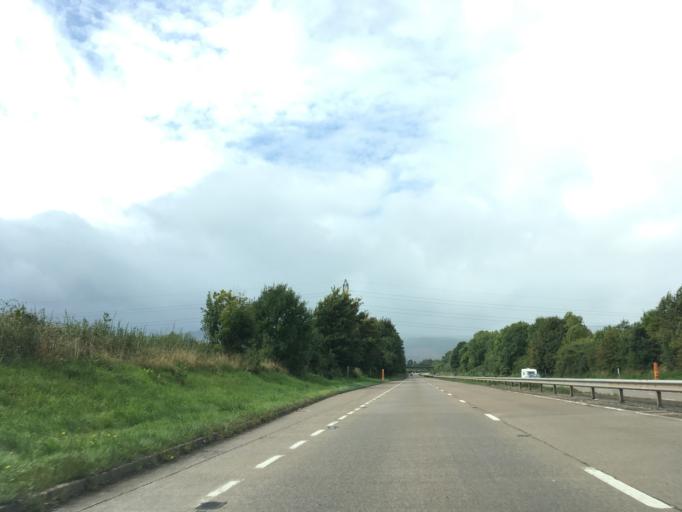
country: GB
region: Wales
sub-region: Monmouthshire
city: Llanarth
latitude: 51.7844
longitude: -2.9633
